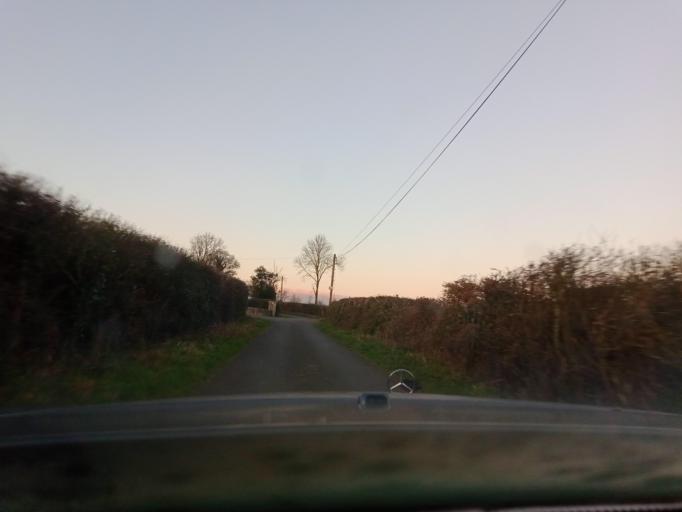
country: IE
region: Leinster
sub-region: Kilkenny
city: Graiguenamanagh
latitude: 52.5703
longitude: -6.9577
